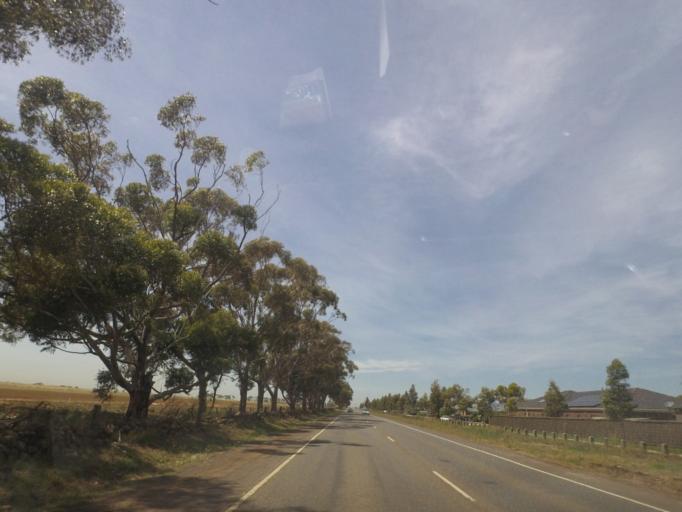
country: AU
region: Victoria
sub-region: Wyndham
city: Wyndham Vale
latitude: -37.8621
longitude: 144.5995
